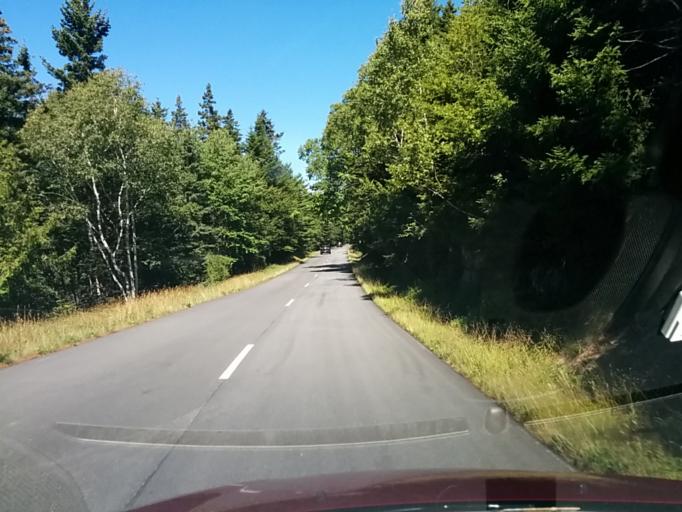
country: US
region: Maine
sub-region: Hancock County
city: Bar Harbor
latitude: 44.2985
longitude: -68.2162
